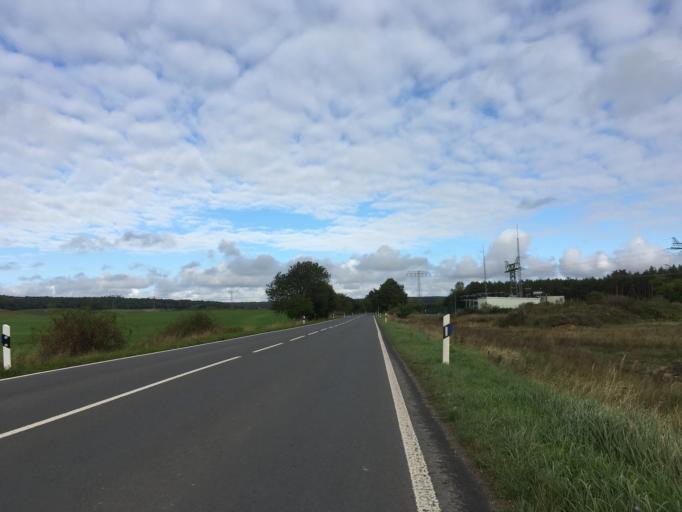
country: DE
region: Brandenburg
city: Oderberg
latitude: 52.8796
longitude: 14.0568
